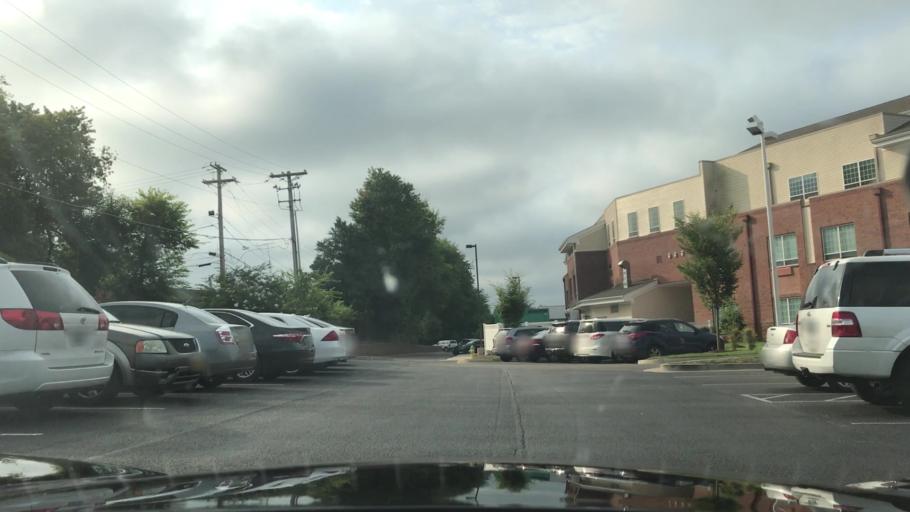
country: US
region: Kentucky
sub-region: Warren County
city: Bowling Green
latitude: 36.9620
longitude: -86.4488
